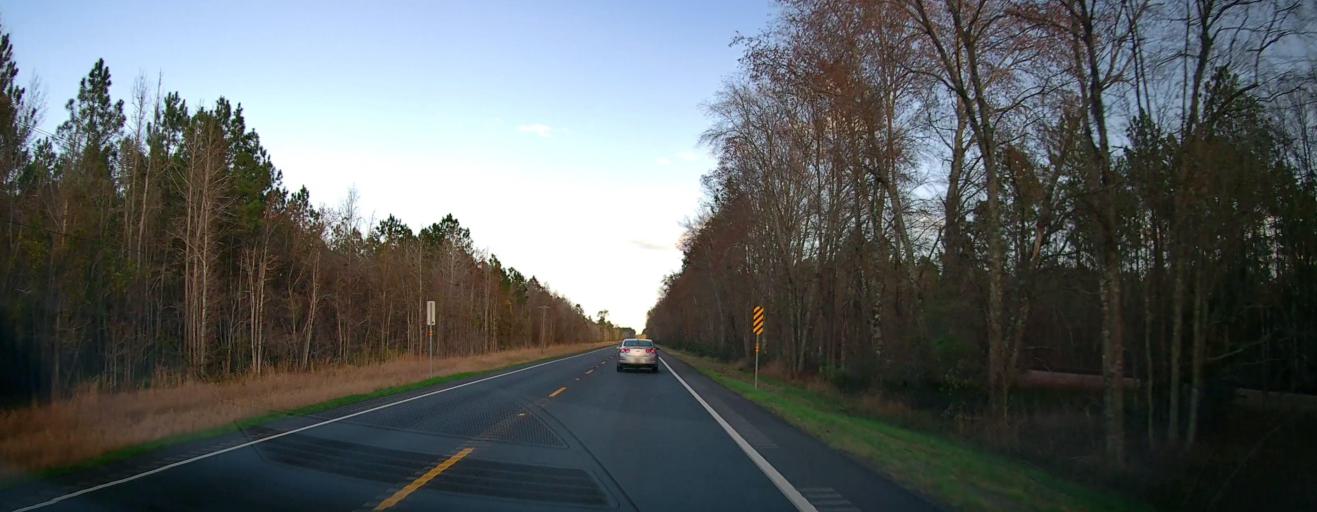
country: US
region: Georgia
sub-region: Bryan County
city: Pembroke
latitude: 32.1333
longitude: -81.5886
